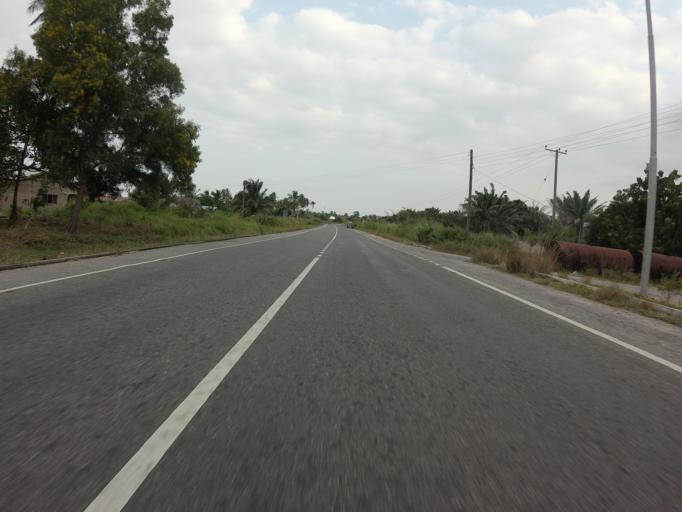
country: GH
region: Volta
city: Ho
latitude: 6.2591
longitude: 0.5494
